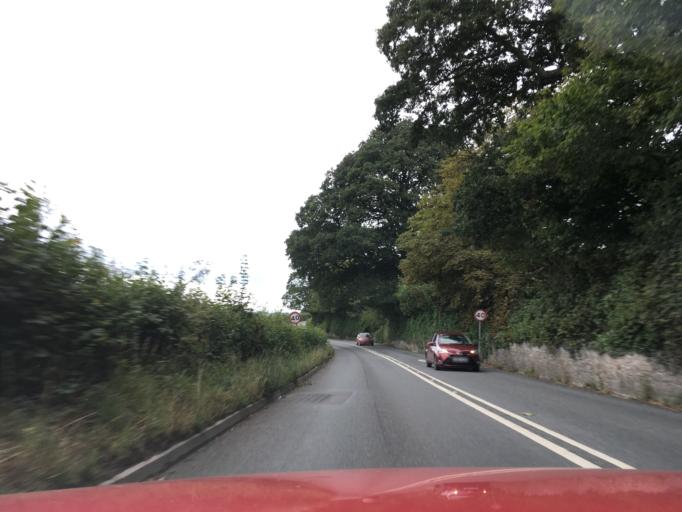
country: GB
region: England
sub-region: Devon
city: Bishopsteignton
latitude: 50.5500
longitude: -3.5493
